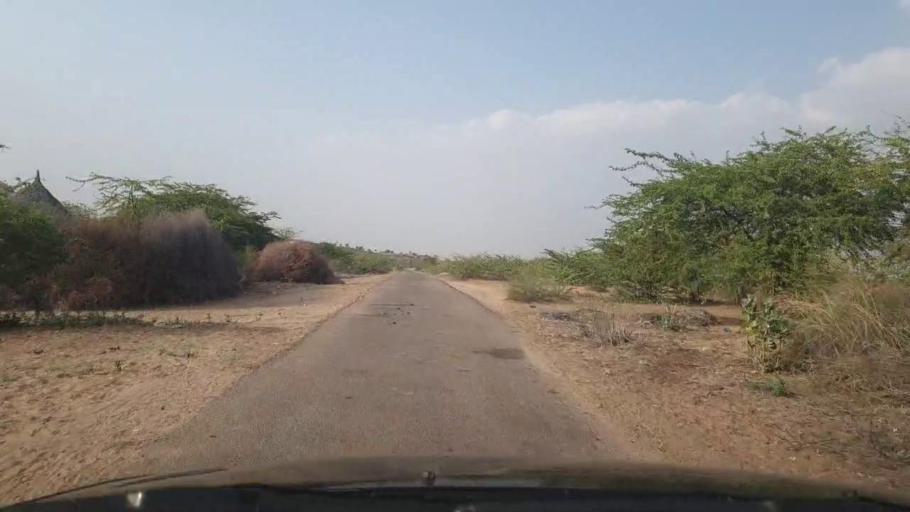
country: PK
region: Sindh
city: Islamkot
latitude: 25.0687
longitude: 70.5656
